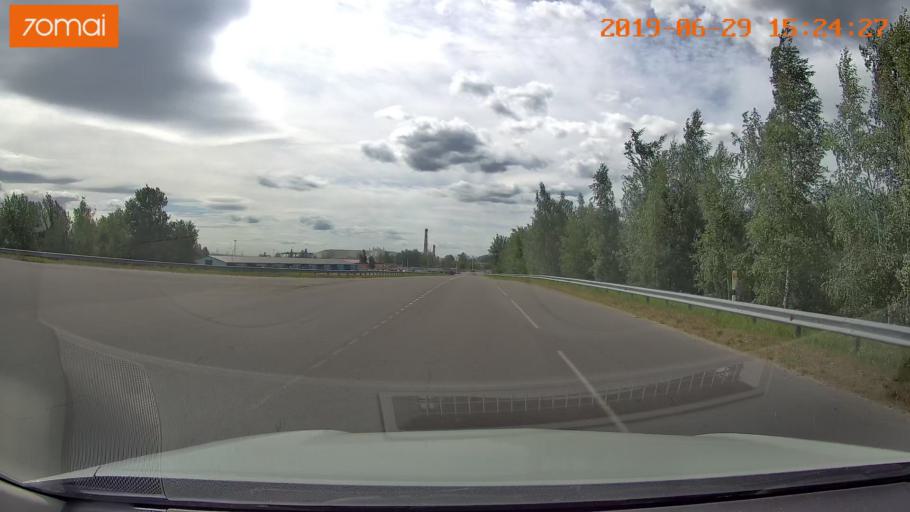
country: BY
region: Brest
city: Mikashevichy
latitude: 52.2103
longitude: 27.4165
